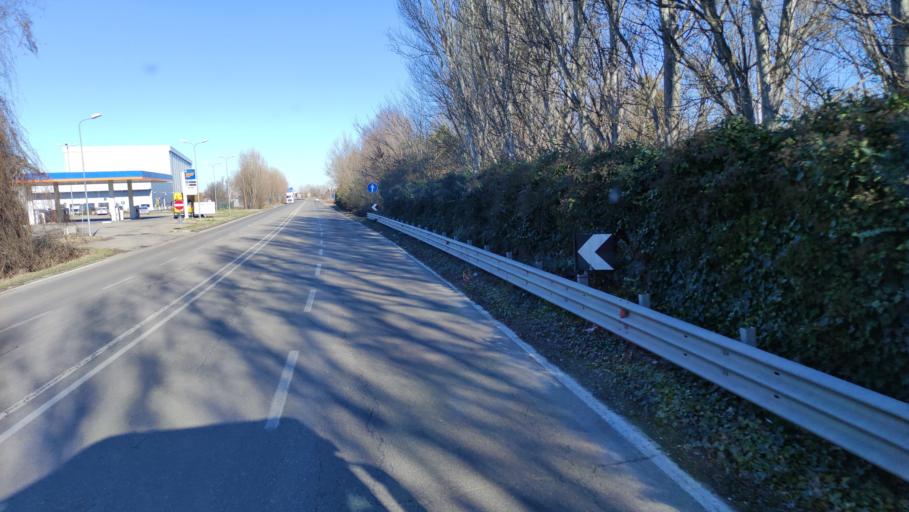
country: IT
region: Emilia-Romagna
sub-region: Provincia di Reggio Emilia
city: Correggio
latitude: 44.7612
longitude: 10.8088
